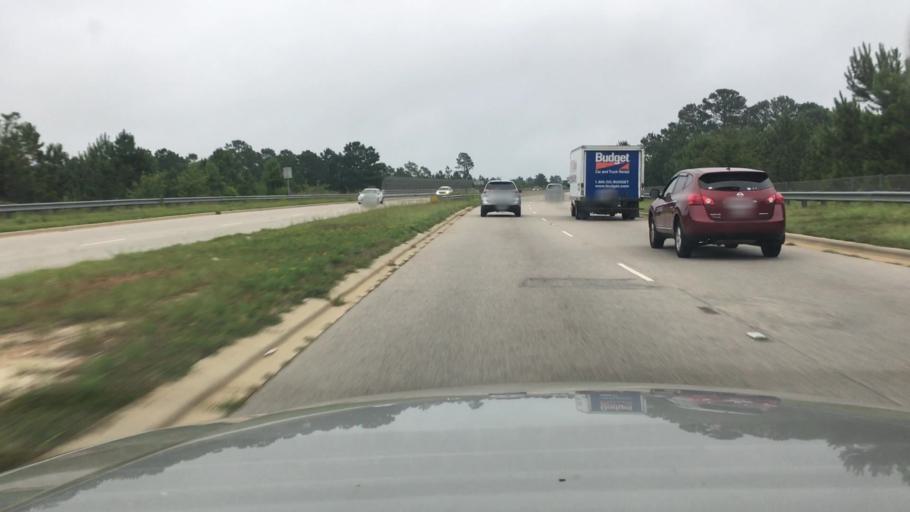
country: US
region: North Carolina
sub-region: Cumberland County
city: Hope Mills
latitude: 34.9901
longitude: -78.9428
